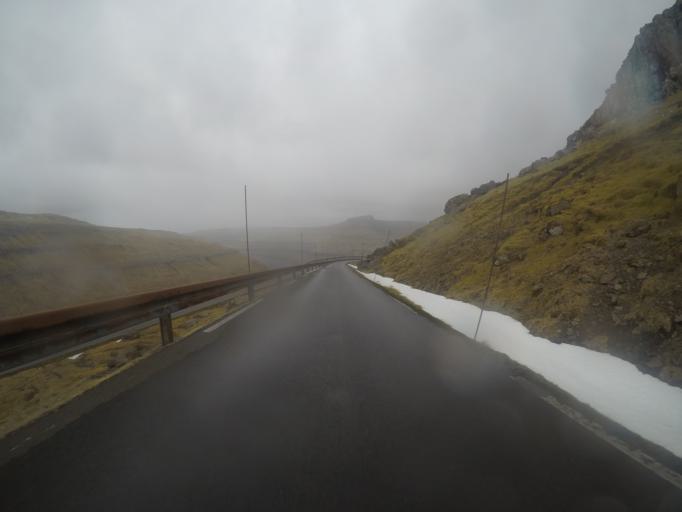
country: FO
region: Streymoy
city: Kollafjordhur
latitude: 62.0819
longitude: -6.9388
